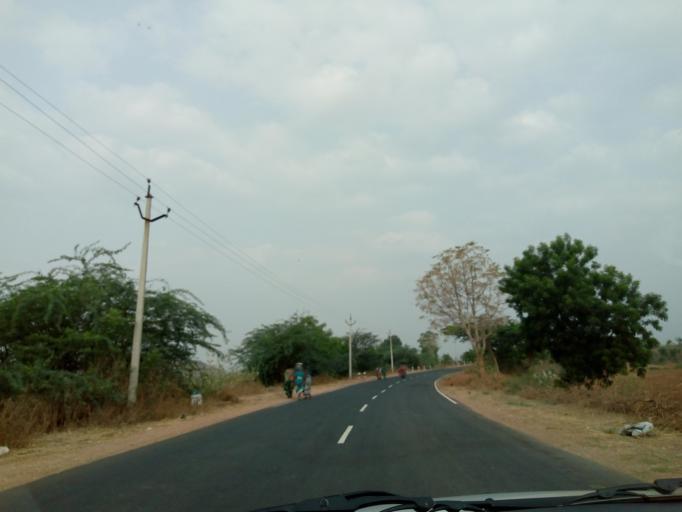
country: IN
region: Andhra Pradesh
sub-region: Prakasam
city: Diguvametta
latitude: 15.3737
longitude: 78.8734
